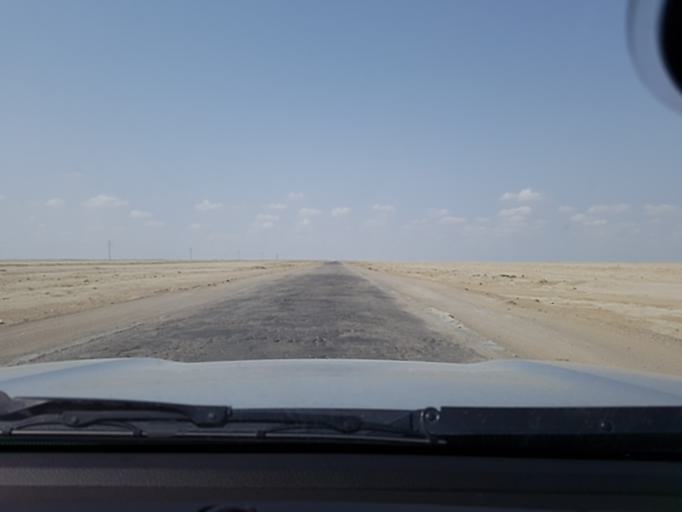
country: TM
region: Balkan
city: Gumdag
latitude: 38.6433
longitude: 54.3777
